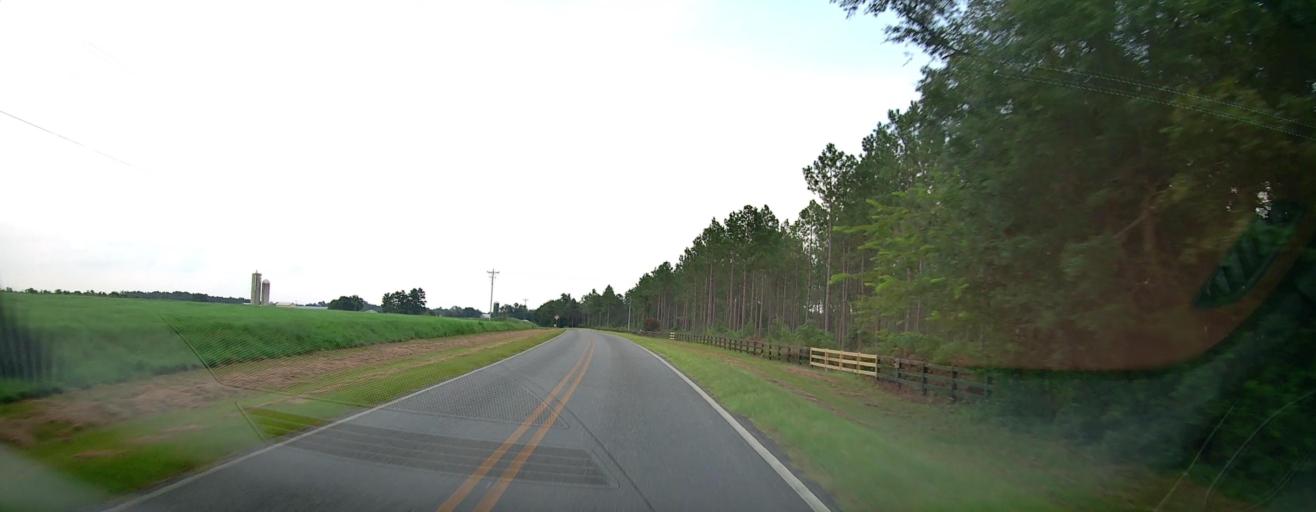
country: US
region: Georgia
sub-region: Laurens County
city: East Dublin
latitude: 32.6354
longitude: -82.8491
